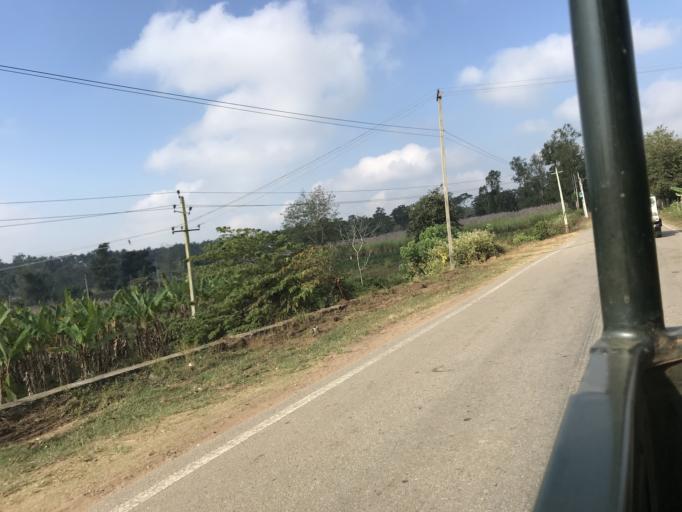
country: IN
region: Karnataka
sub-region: Mysore
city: Heggadadevankote
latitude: 11.9475
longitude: 76.2499
